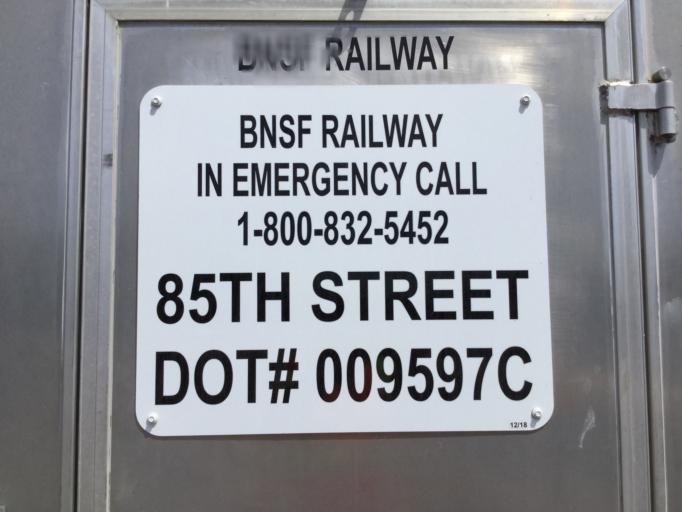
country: US
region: Kansas
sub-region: Butler County
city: Augusta
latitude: 37.7013
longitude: -96.9431
